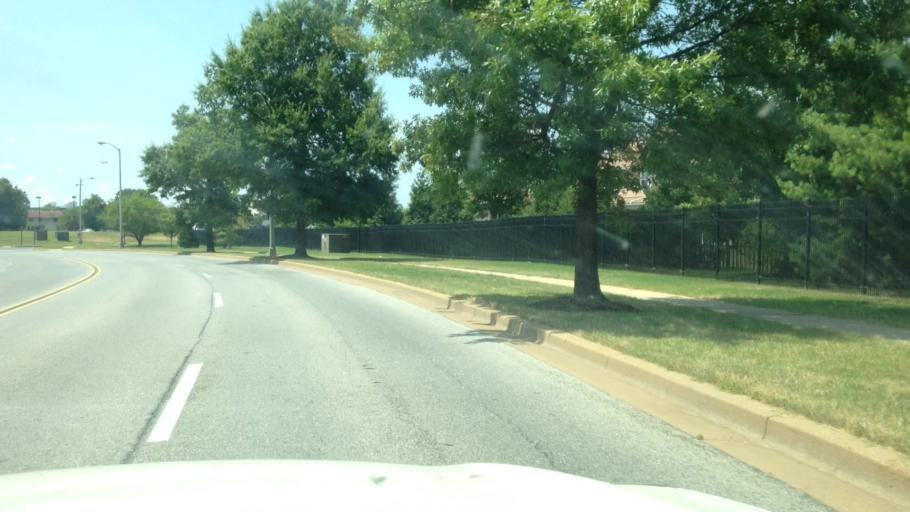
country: US
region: Maryland
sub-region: Prince George's County
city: Glassmanor
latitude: 38.8353
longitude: -77.0205
